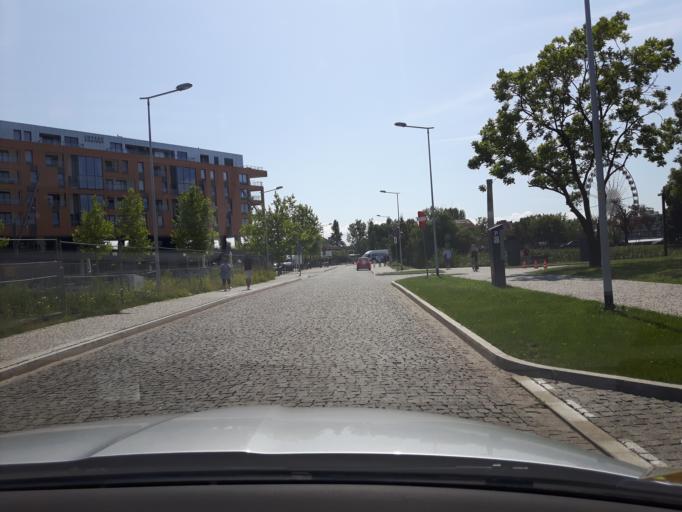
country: PL
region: Pomeranian Voivodeship
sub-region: Gdansk
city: Gdansk
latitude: 54.3556
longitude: 18.6617
